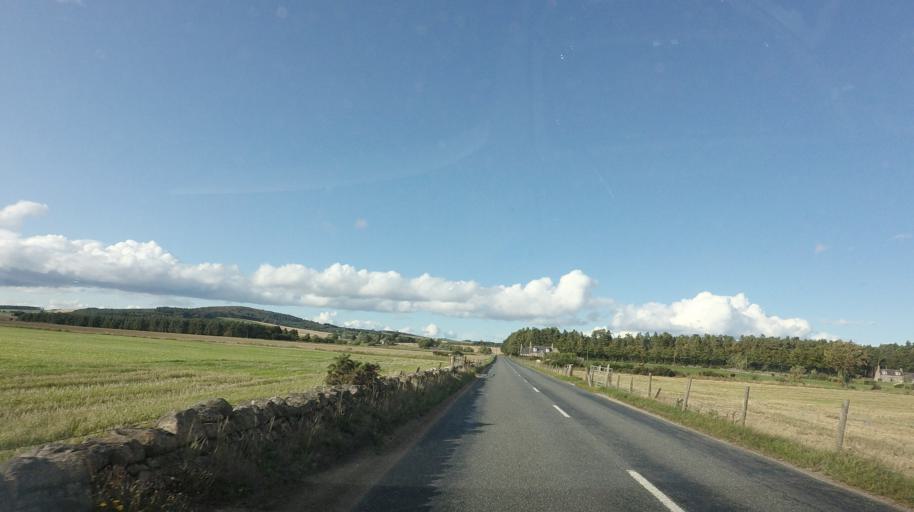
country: GB
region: Scotland
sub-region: Aberdeenshire
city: Banchory
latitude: 57.1282
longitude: -2.4276
